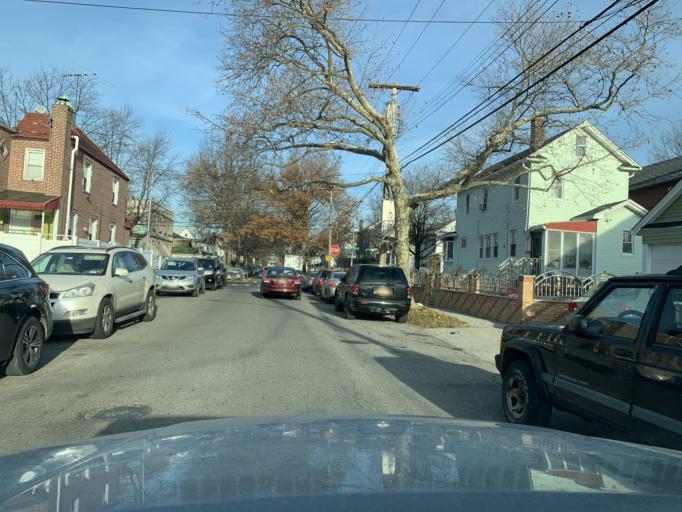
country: US
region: New York
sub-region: Queens County
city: Jamaica
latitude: 40.6950
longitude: -73.7794
